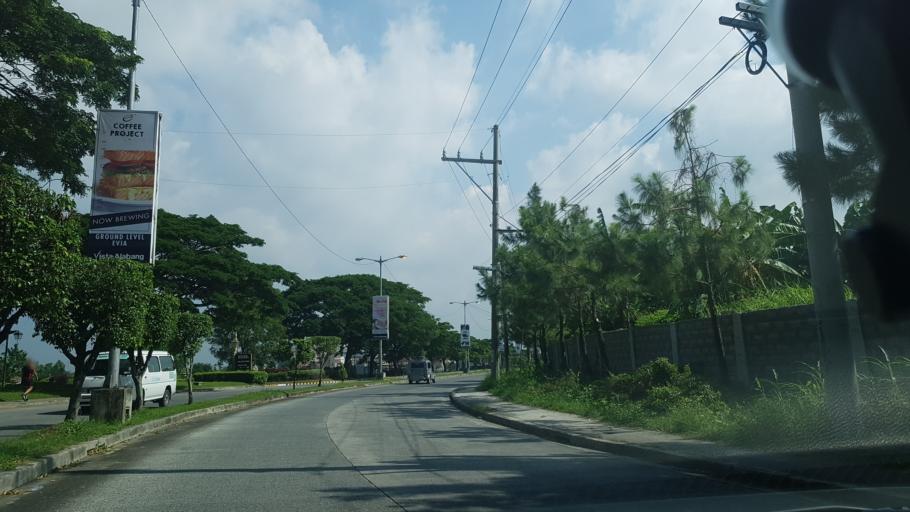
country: PH
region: Calabarzon
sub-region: Province of Laguna
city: San Pedro
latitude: 14.3694
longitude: 121.0100
